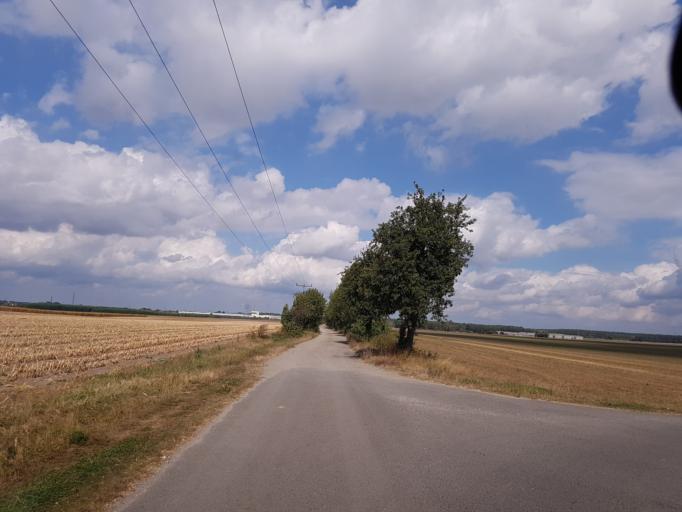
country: DE
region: Brandenburg
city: Finsterwalde
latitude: 51.6213
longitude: 13.7580
